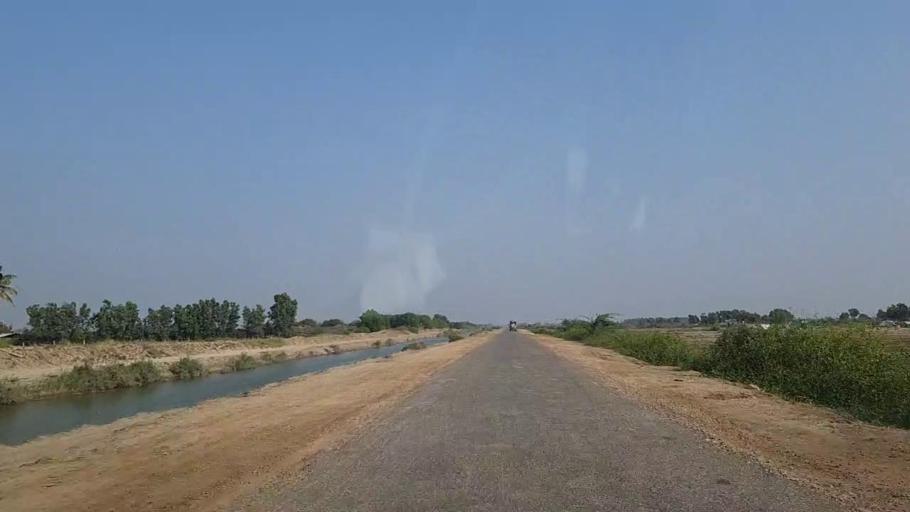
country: PK
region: Sindh
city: Mirpur Sakro
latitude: 24.6368
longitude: 67.5989
